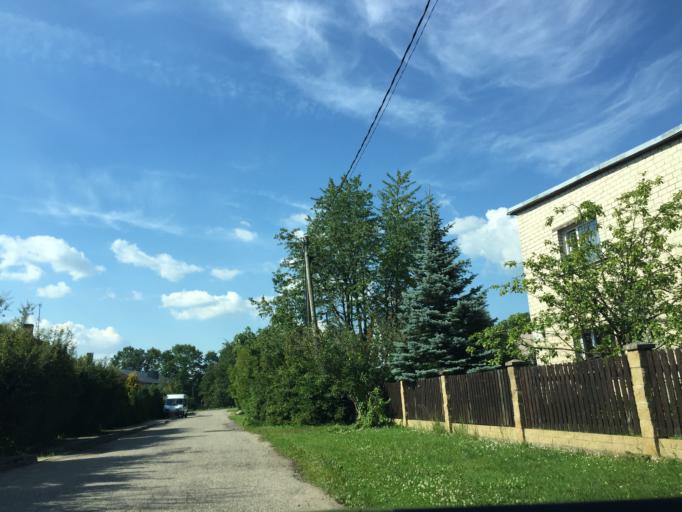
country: LV
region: Sigulda
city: Sigulda
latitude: 57.1520
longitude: 24.8629
